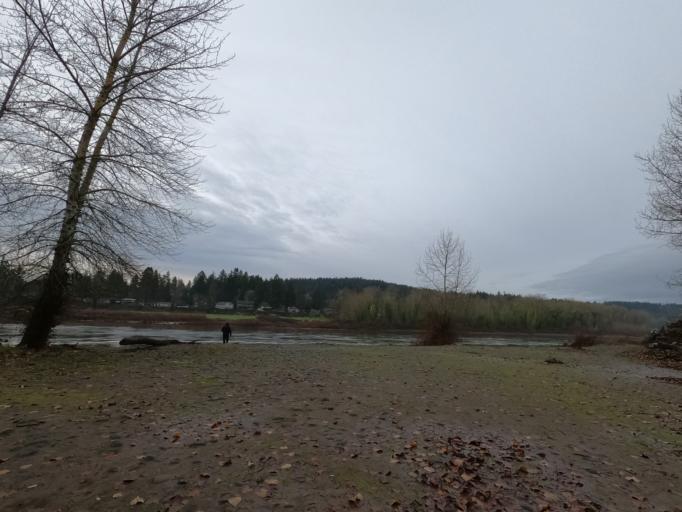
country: US
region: Oregon
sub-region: Clackamas County
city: West Linn
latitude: 45.3718
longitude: -122.6055
